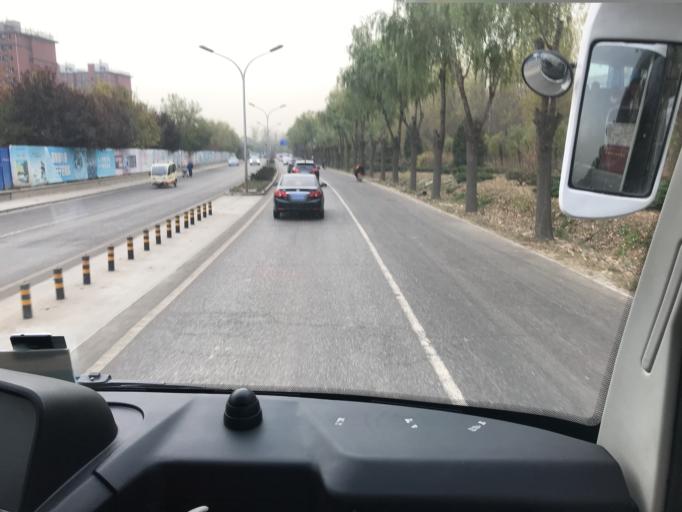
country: CN
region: Beijing
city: Sujiatuo
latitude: 40.0943
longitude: 116.2085
